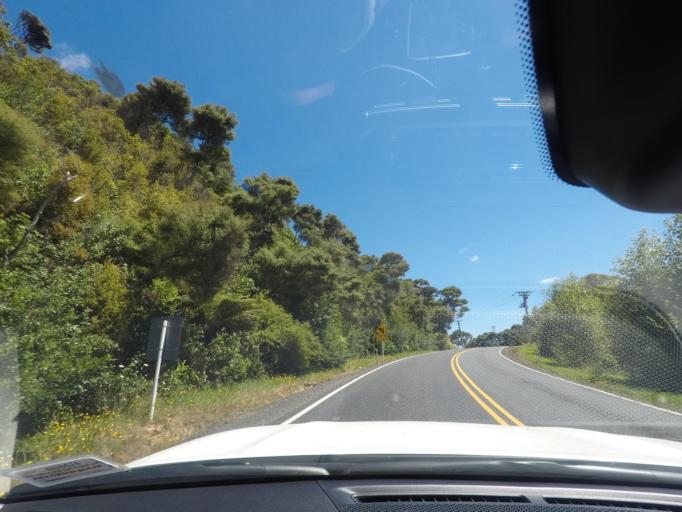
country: NZ
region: Auckland
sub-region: Auckland
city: Parakai
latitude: -36.5791
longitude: 174.3261
